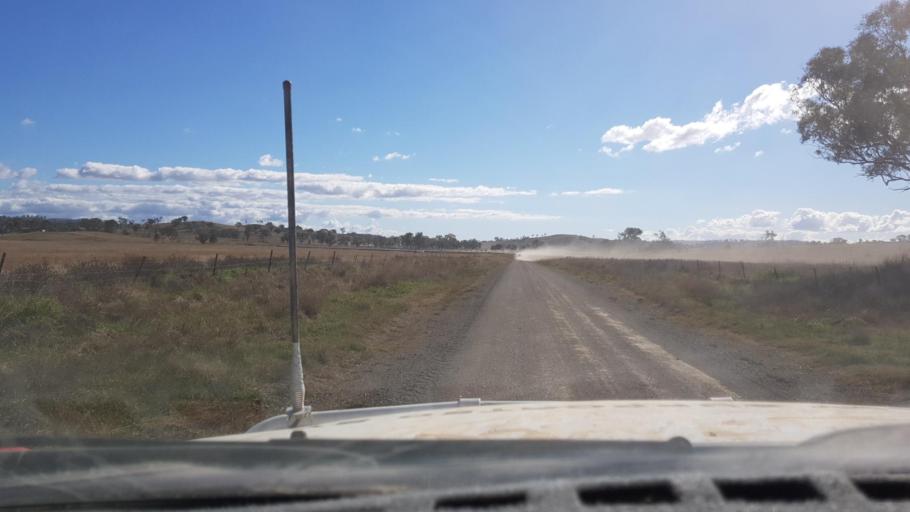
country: AU
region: New South Wales
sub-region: Narrabri
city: Blair Athol
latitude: -30.5129
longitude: 150.4445
